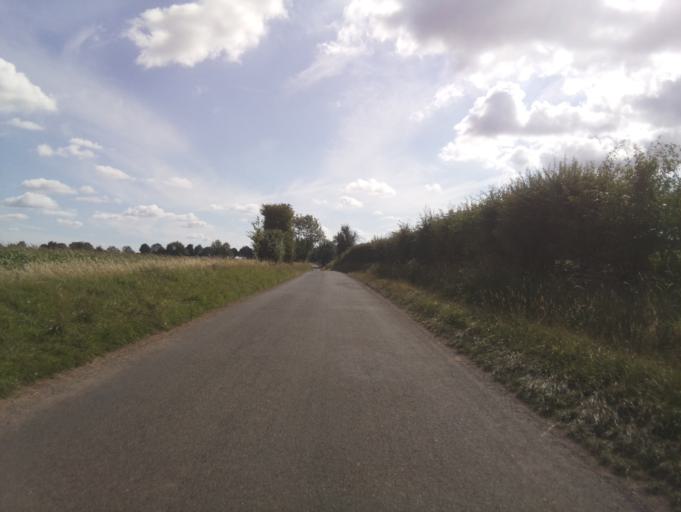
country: GB
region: England
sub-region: Gloucestershire
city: Coates
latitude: 51.6975
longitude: -2.0538
